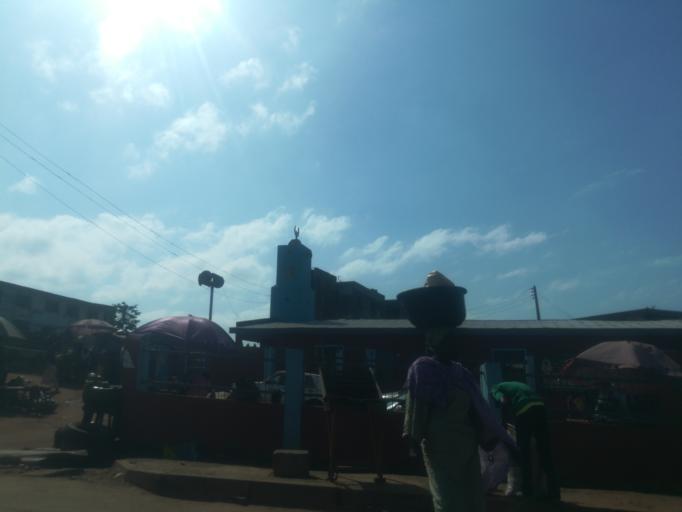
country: NG
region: Oyo
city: Ibadan
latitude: 7.4122
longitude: 3.9537
